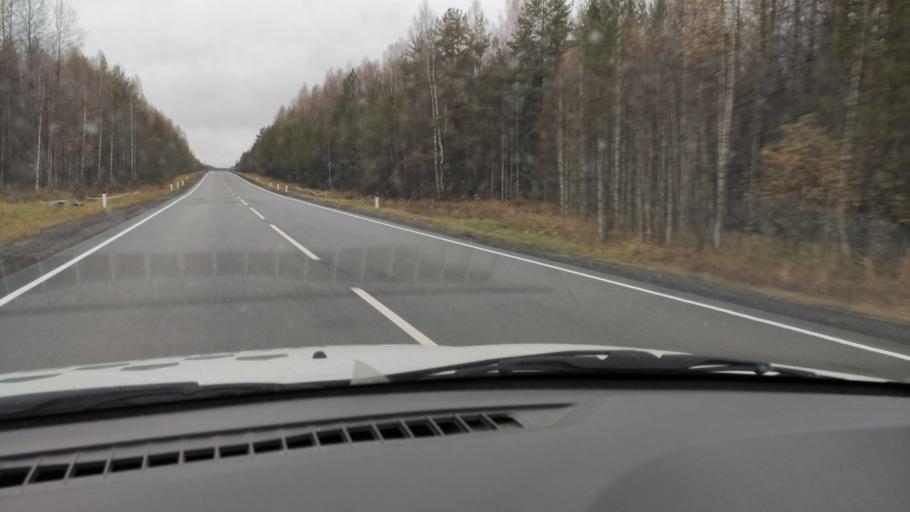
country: RU
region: Kirov
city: Chernaya Kholunitsa
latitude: 58.8619
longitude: 51.6049
